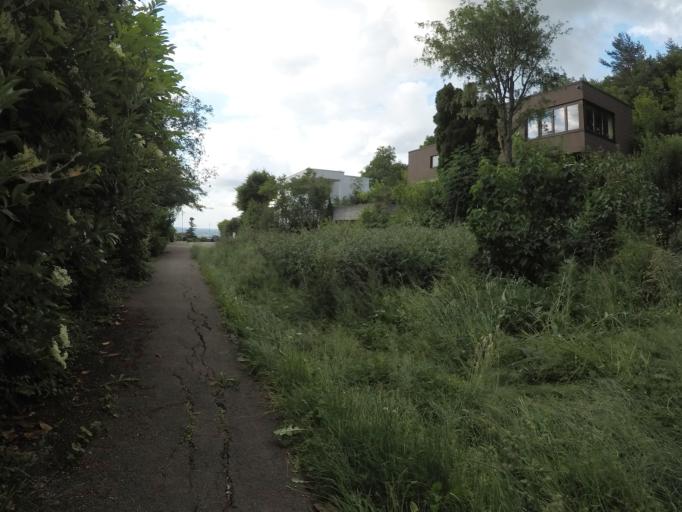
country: DE
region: Baden-Wuerttemberg
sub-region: Tuebingen Region
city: Pfullingen
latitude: 48.4463
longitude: 9.2170
